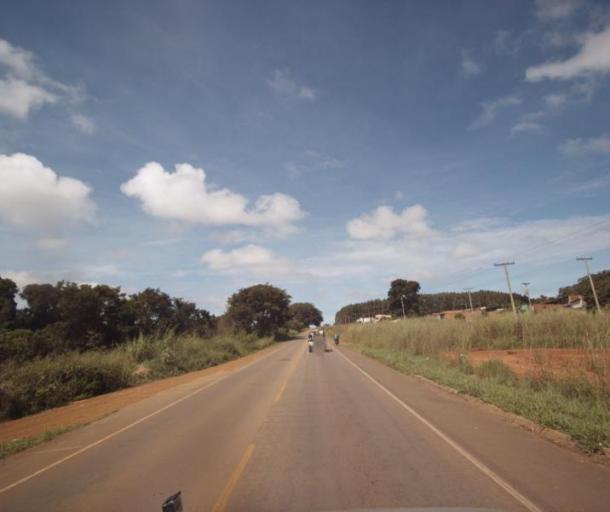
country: BR
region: Goias
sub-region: Anapolis
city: Anapolis
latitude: -16.2745
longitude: -48.9409
